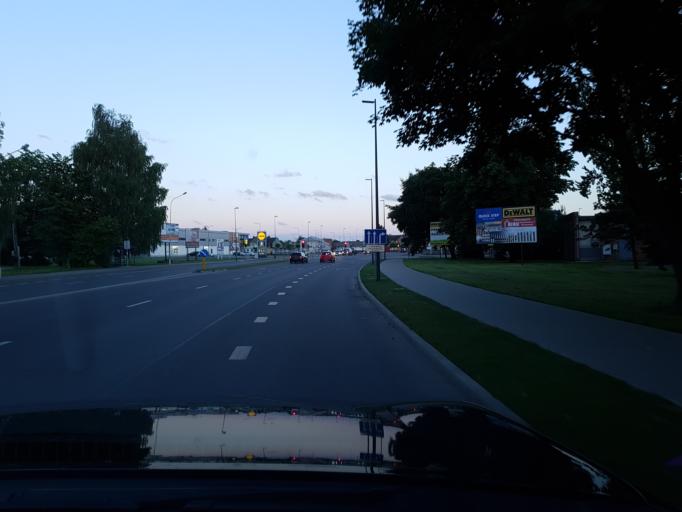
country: LT
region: Marijampoles apskritis
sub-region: Marijampole Municipality
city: Marijampole
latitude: 54.5584
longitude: 23.3544
